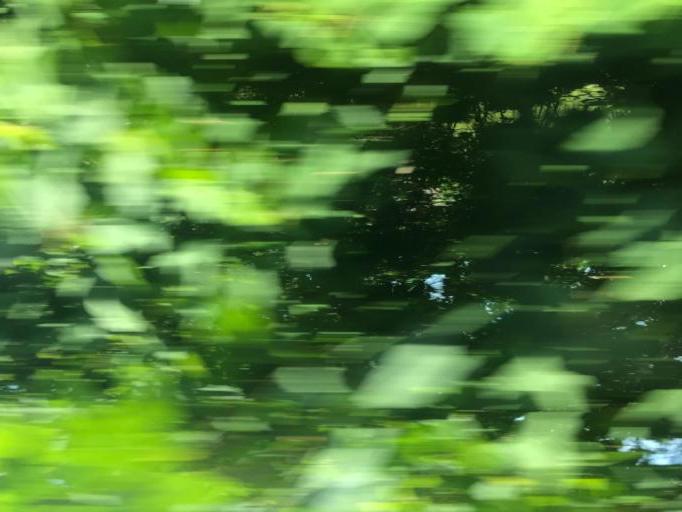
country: JP
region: Niigata
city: Kameda-honcho
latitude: 37.9218
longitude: 139.1554
